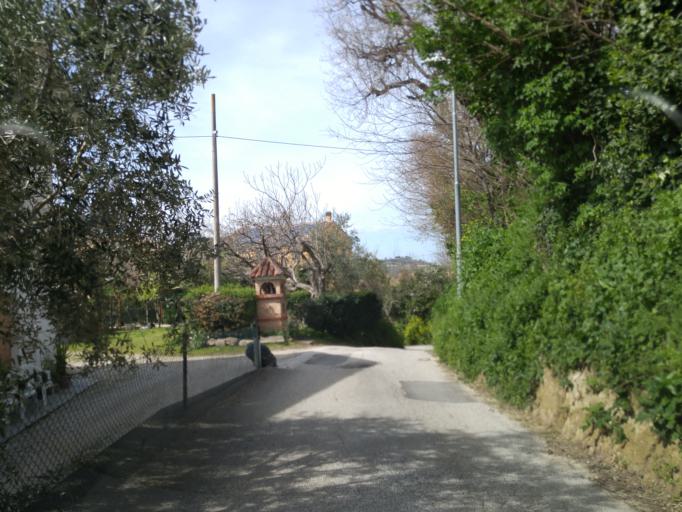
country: IT
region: The Marches
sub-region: Provincia di Pesaro e Urbino
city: Cartoceto
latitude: 43.7703
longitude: 12.8926
